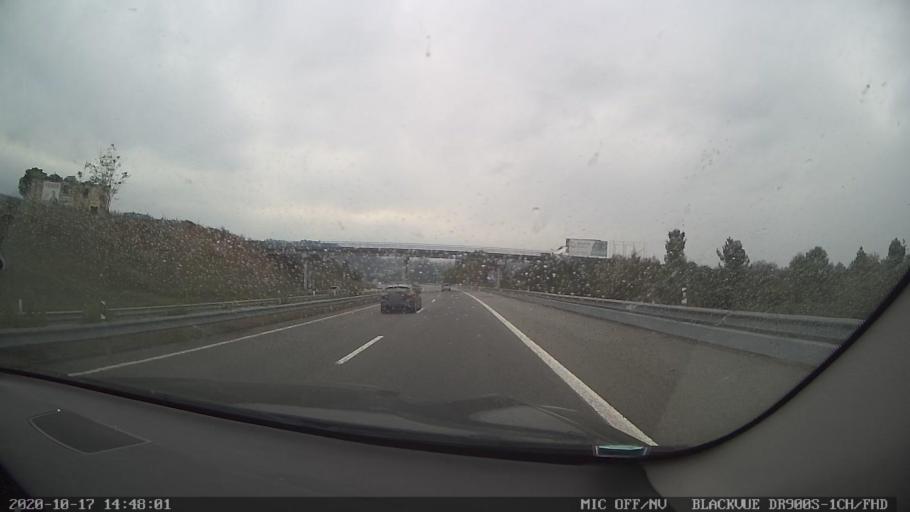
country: PT
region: Braga
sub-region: Barcelos
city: Galegos
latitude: 41.5379
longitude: -8.5356
